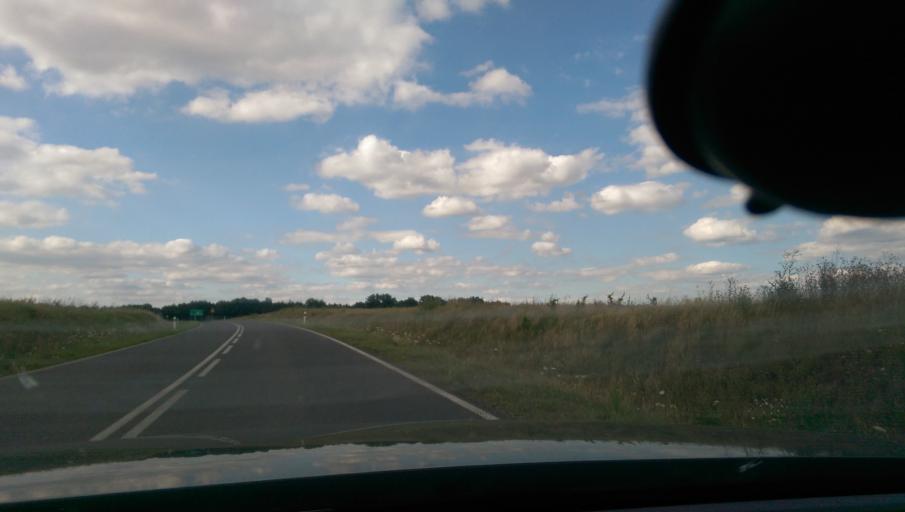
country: PL
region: Lubusz
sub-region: Powiat slubicki
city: Osno Lubuskie
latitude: 52.4524
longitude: 14.8951
